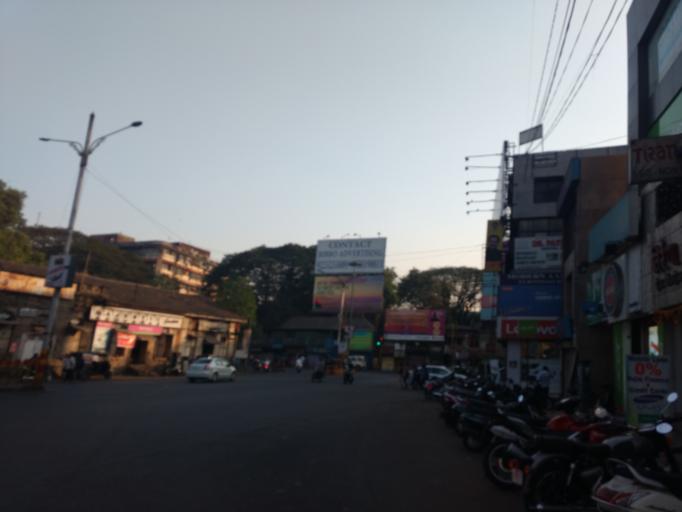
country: IN
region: Maharashtra
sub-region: Pune Division
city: Pune
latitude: 18.5076
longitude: 73.8792
